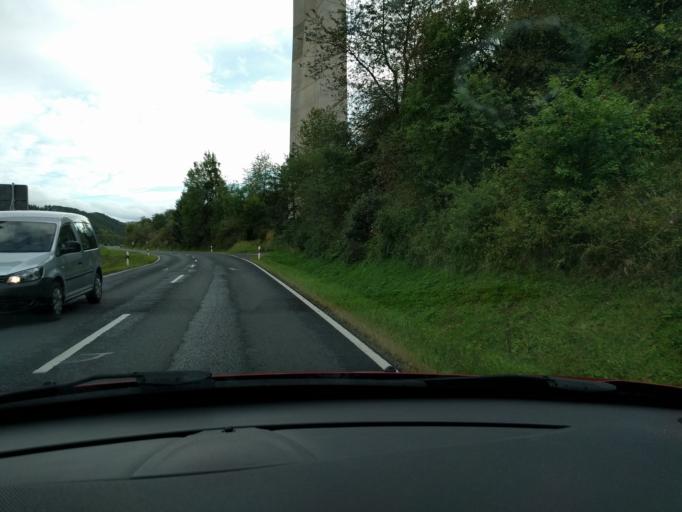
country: DE
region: Thuringia
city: Dillstadt
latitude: 50.5982
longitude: 10.5212
